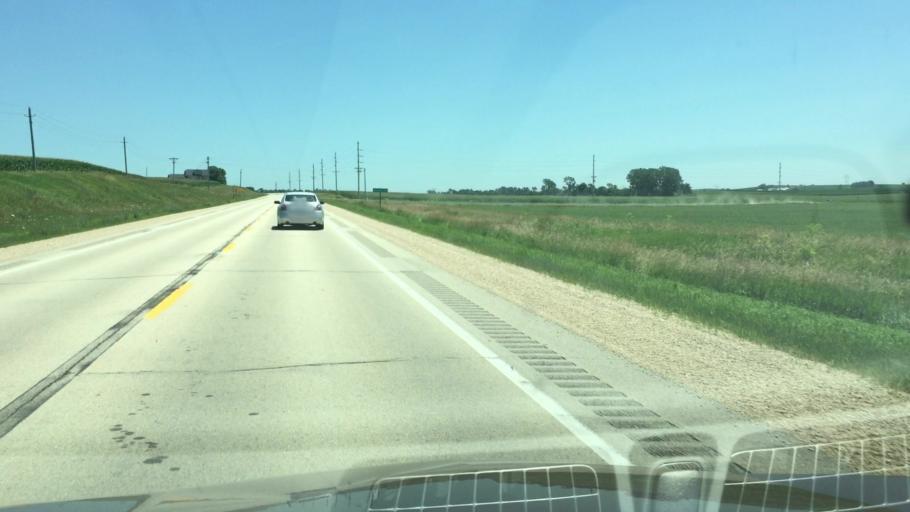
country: US
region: Iowa
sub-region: Jackson County
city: Maquoketa
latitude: 42.0680
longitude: -90.7850
